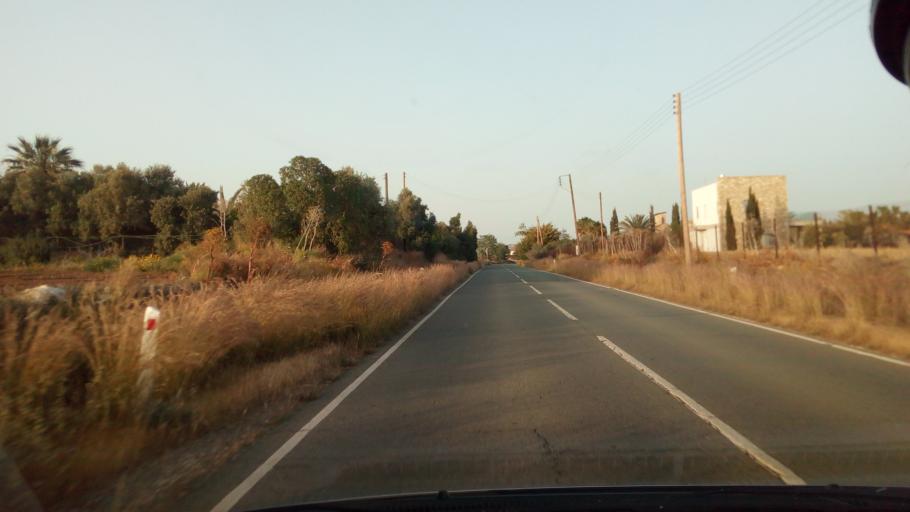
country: CY
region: Larnaka
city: Kofinou
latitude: 34.7356
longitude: 33.3721
